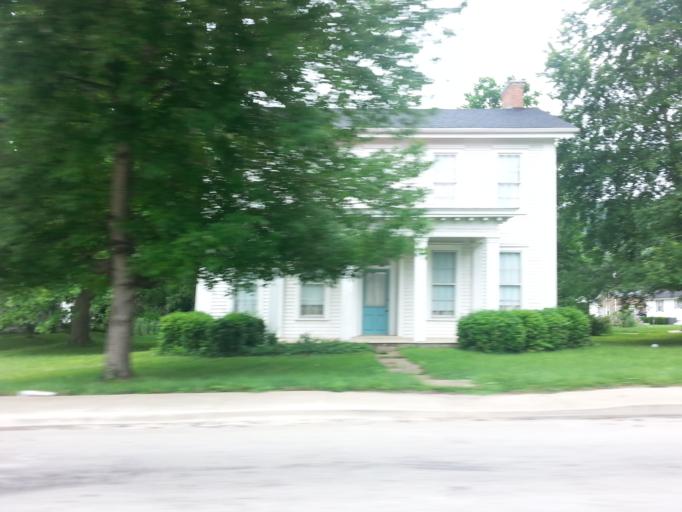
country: US
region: Ohio
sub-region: Brown County
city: Ripley
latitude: 38.7400
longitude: -83.8419
